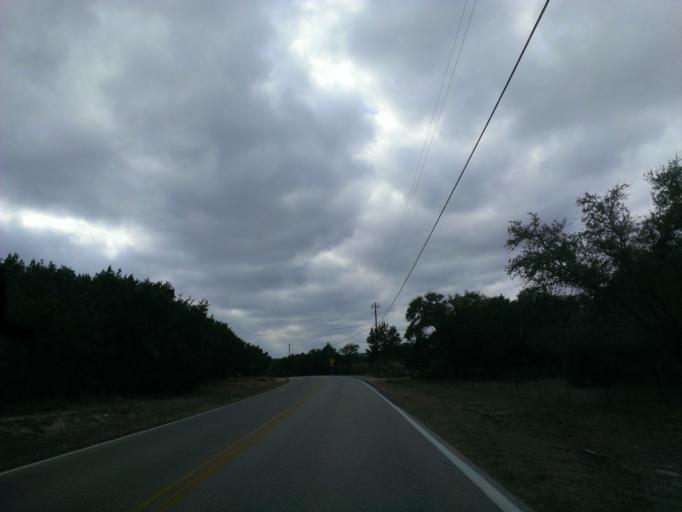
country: US
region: Texas
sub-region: Travis County
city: Briarcliff
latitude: 30.3760
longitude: -98.0863
